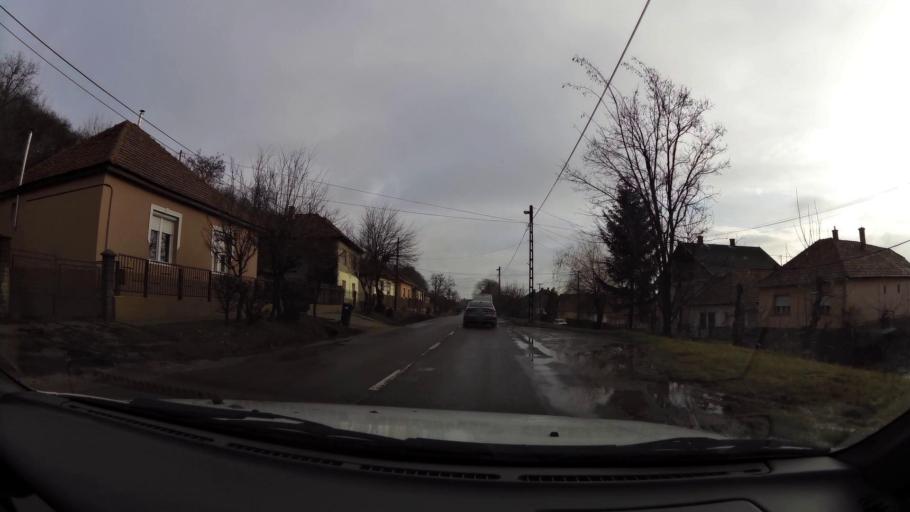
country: HU
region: Borsod-Abauj-Zemplen
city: Mucsony
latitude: 48.2721
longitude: 20.6727
